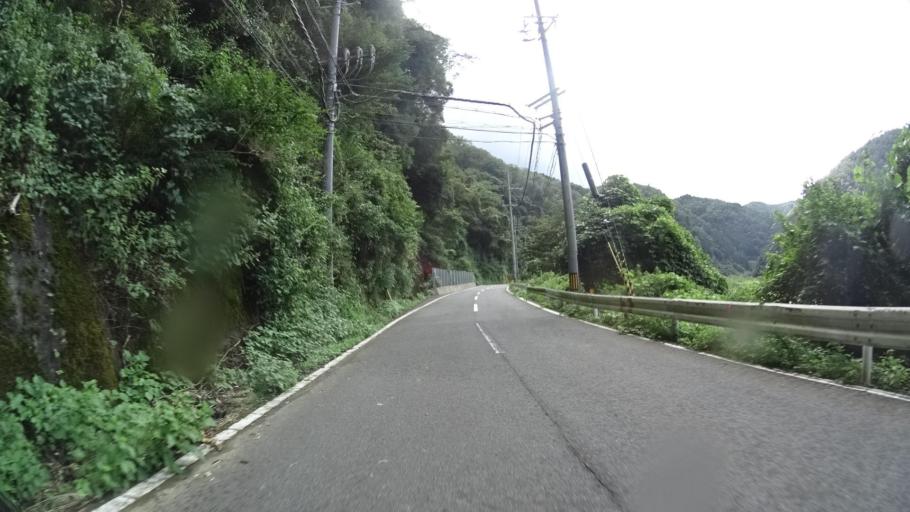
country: JP
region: Mie
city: Ueno-ebisumachi
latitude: 34.7645
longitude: 136.0022
